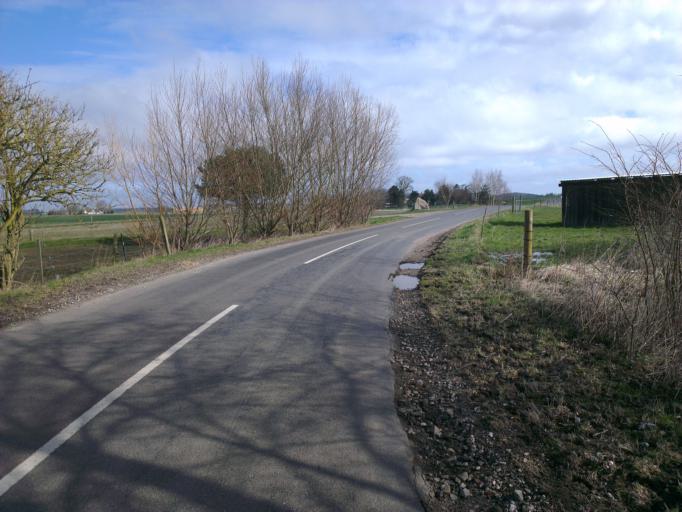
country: DK
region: Capital Region
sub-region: Hillerod Kommune
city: Skaevinge
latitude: 55.8742
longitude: 12.1175
